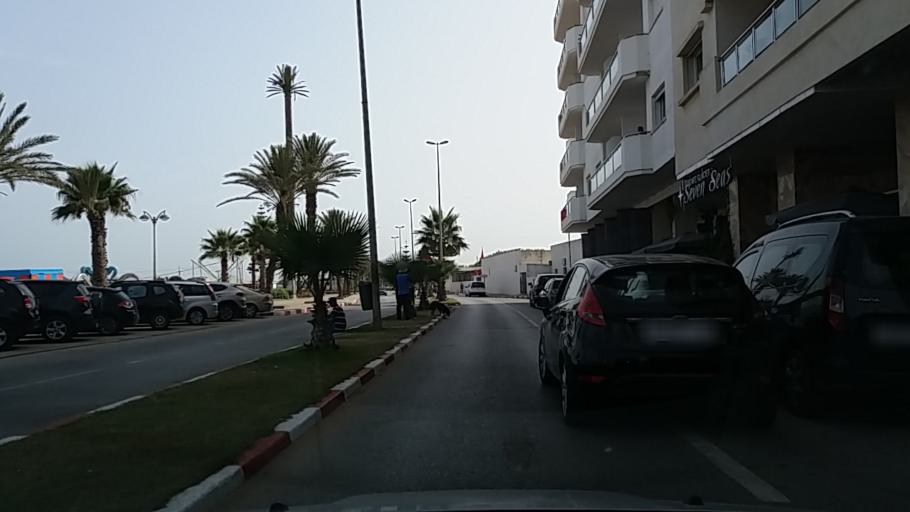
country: MA
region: Tanger-Tetouan
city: Asilah
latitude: 35.4711
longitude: -6.0306
